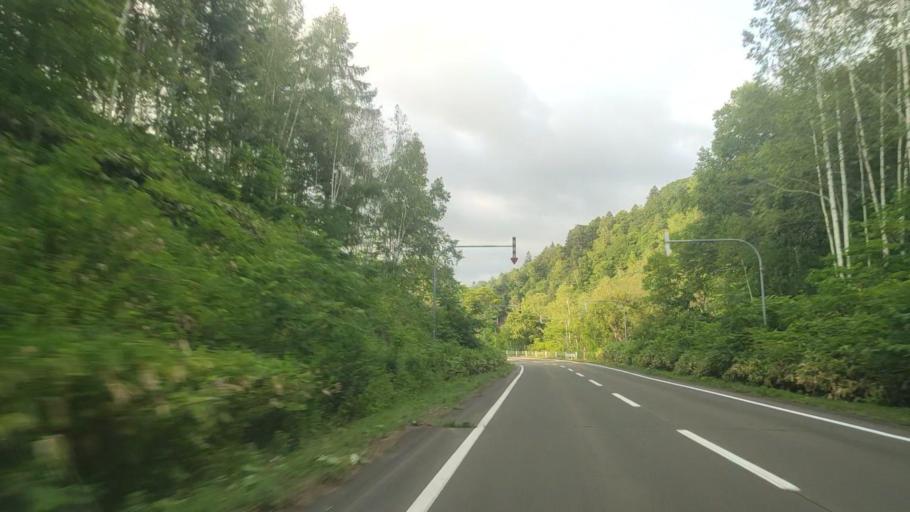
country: JP
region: Hokkaido
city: Bibai
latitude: 43.1370
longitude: 142.0964
